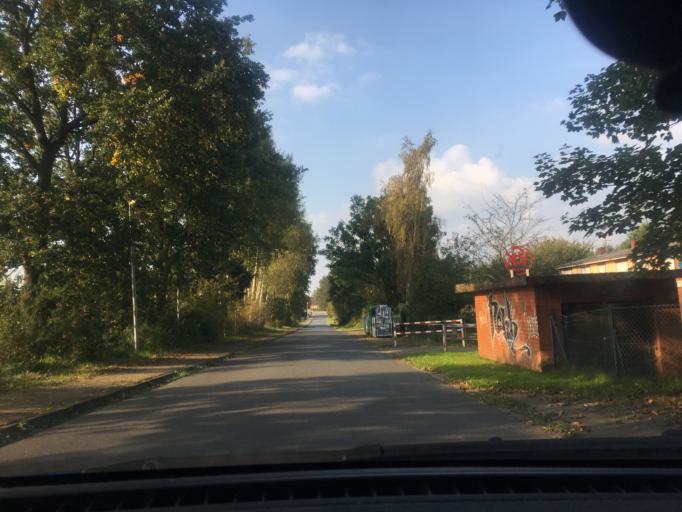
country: DE
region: Lower Saxony
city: Vastorf
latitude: 53.1927
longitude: 10.5492
